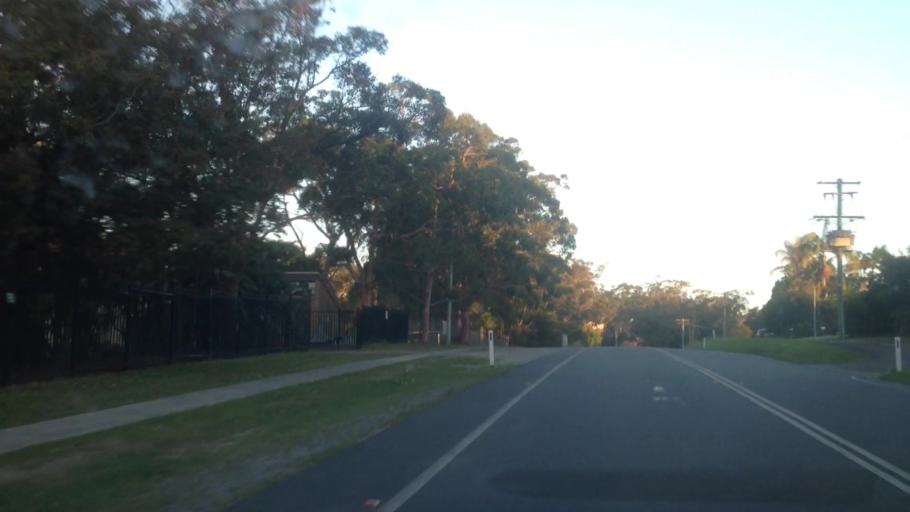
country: AU
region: New South Wales
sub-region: Lake Macquarie Shire
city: Dora Creek
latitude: -33.1056
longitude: 151.4821
